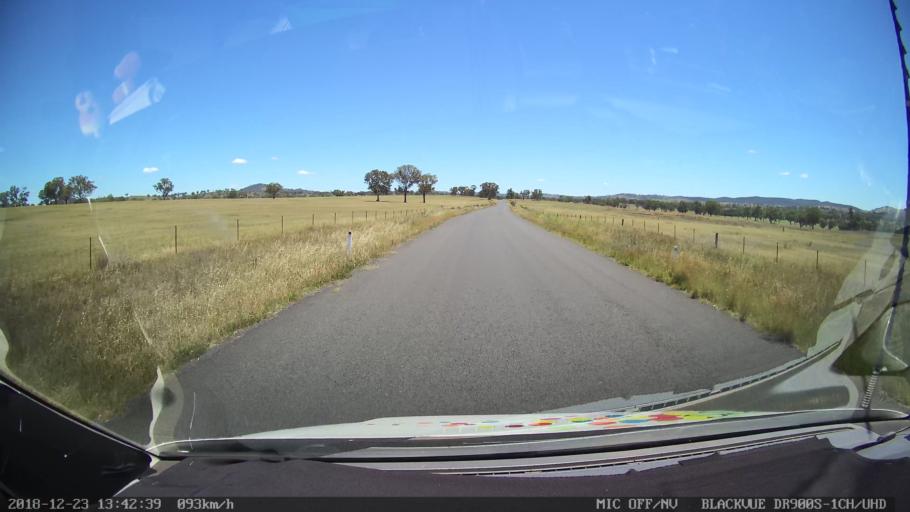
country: AU
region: New South Wales
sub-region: Armidale Dumaresq
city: Armidale
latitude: -30.4792
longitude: 151.1604
